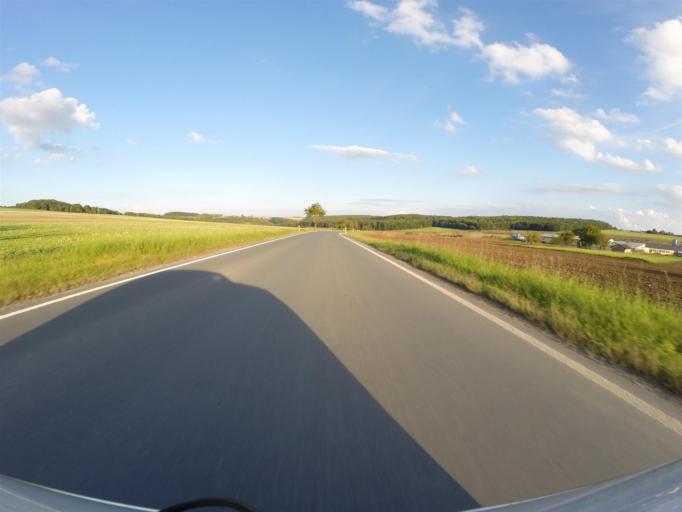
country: DE
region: Thuringia
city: Bucha
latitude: 50.8816
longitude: 11.5156
